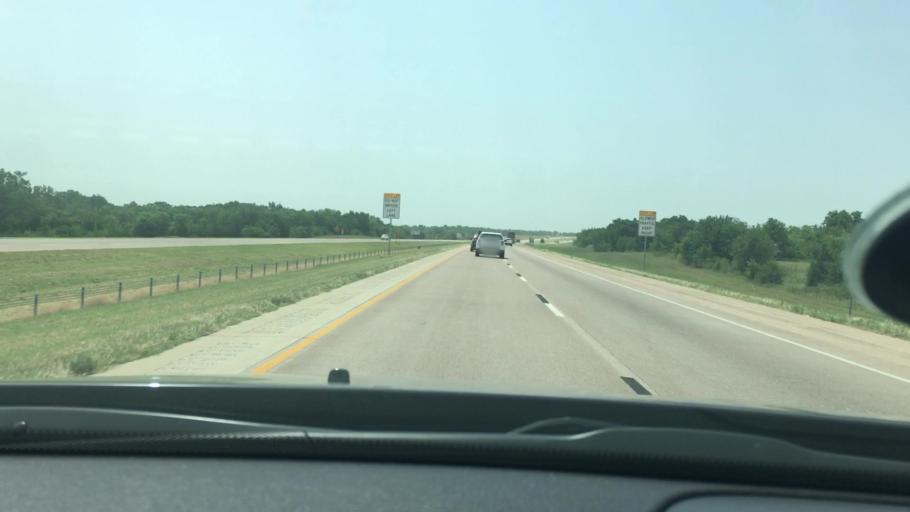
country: US
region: Oklahoma
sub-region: Garvin County
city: Pauls Valley
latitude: 34.6961
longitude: -97.2366
